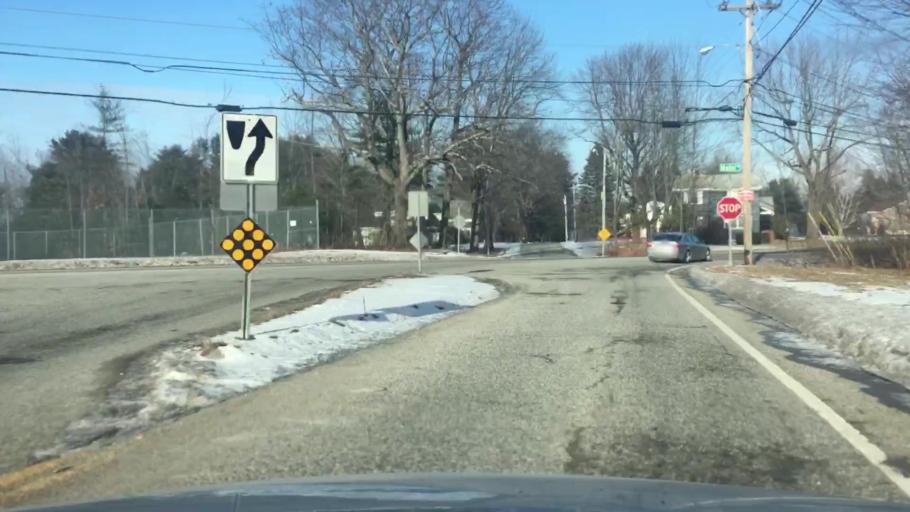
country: US
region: Maine
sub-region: Androscoggin County
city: Minot
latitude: 44.0506
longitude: -70.2758
